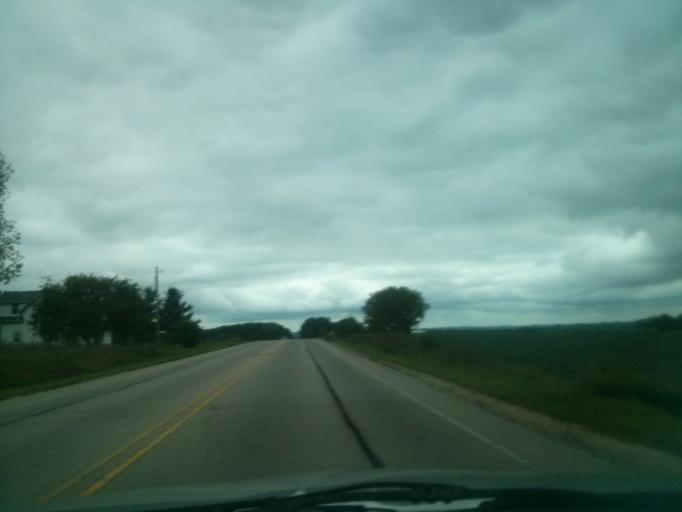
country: US
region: Wisconsin
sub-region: Pierce County
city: Spring Valley
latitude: 44.8316
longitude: -92.3250
